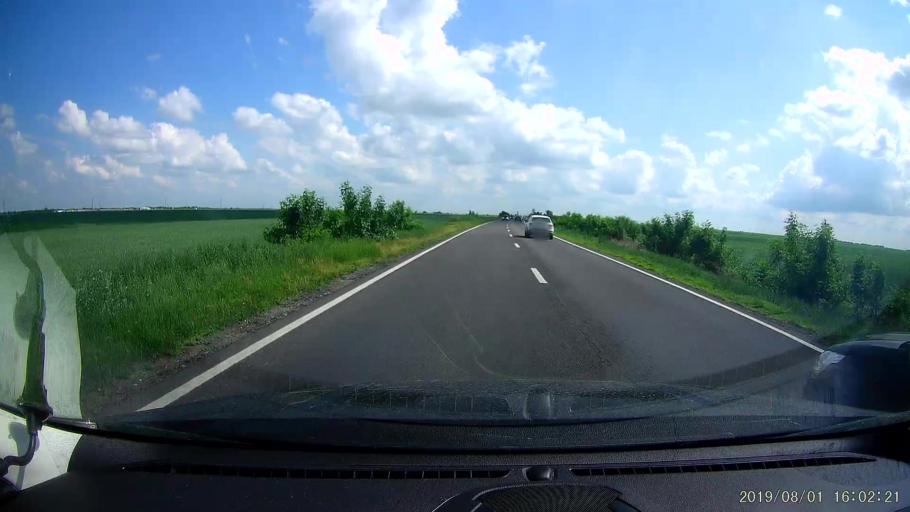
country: RO
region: Ialomita
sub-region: Comuna Ciulnita
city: Ciulnita
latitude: 44.4912
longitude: 27.3877
